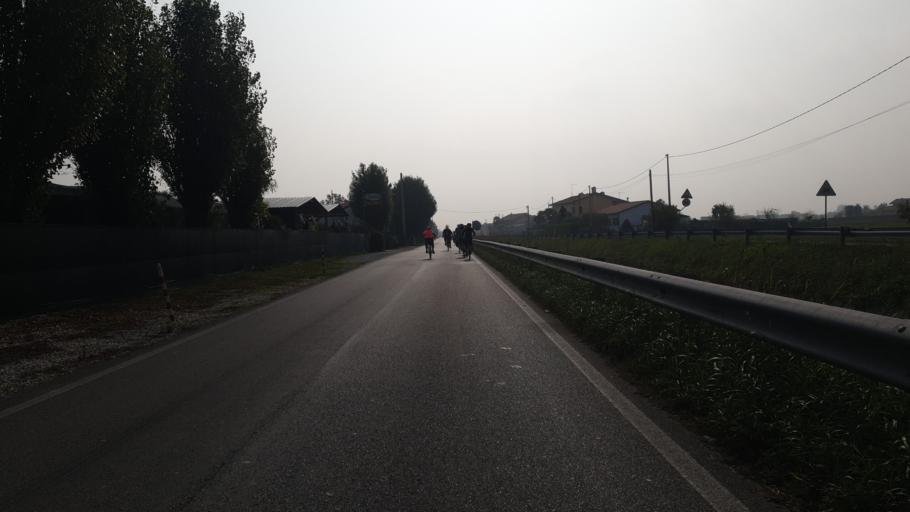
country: IT
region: Veneto
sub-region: Provincia di Padova
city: Corte
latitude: 45.3060
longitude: 12.0743
